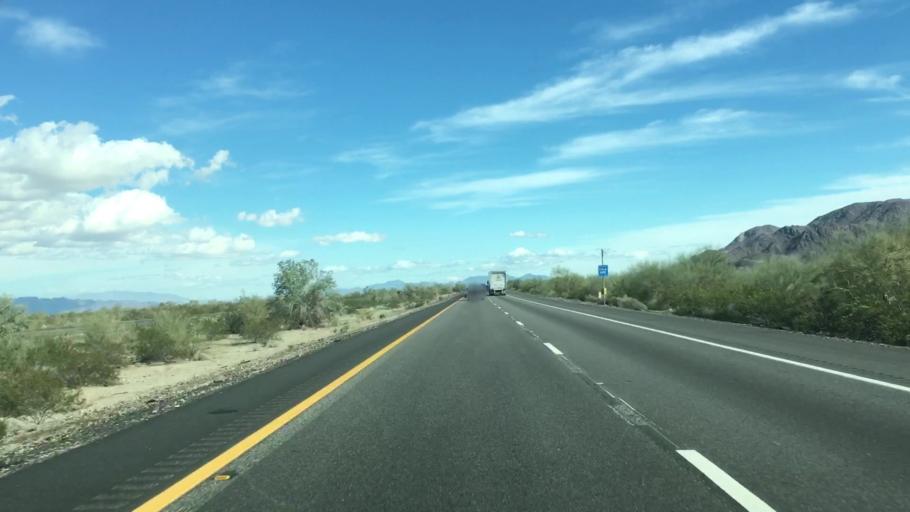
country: US
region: California
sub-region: Imperial County
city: Niland
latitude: 33.6834
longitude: -115.5371
